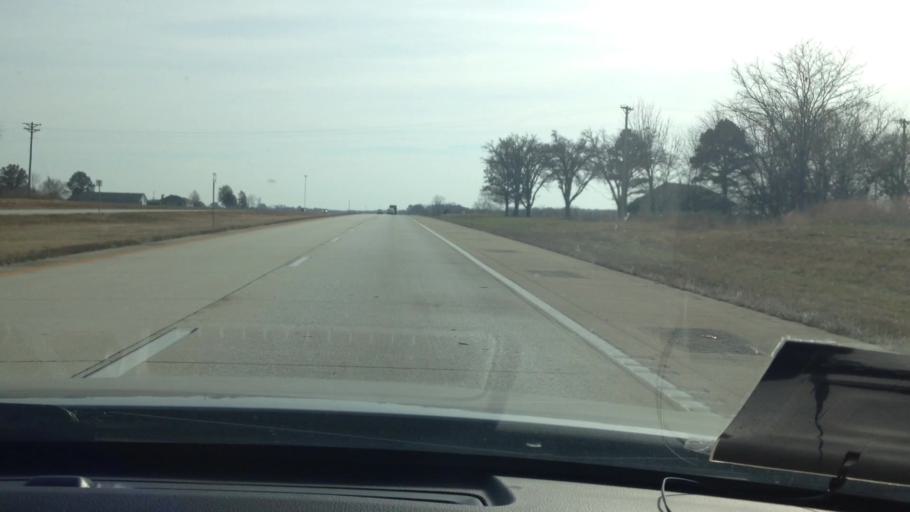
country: US
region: Missouri
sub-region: Henry County
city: Clinton
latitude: 38.4587
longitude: -93.9675
